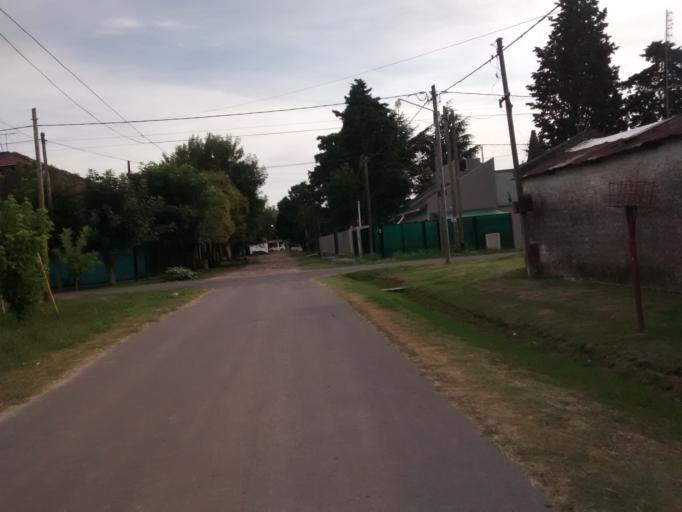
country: AR
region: Buenos Aires
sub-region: Partido de La Plata
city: La Plata
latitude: -34.8532
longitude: -58.0950
